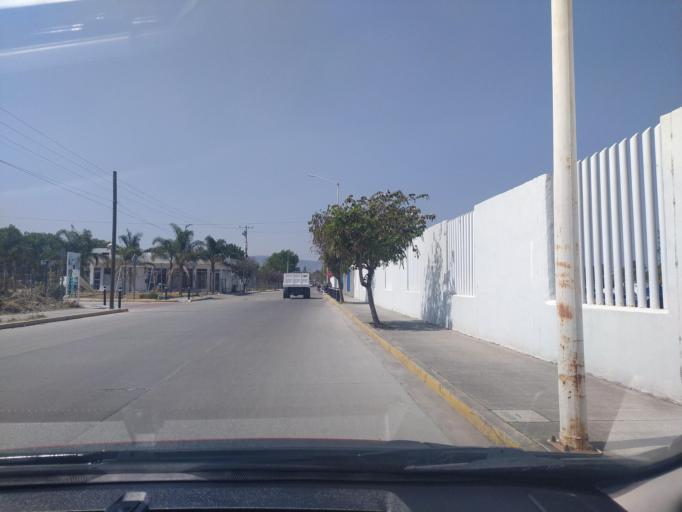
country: MX
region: Guanajuato
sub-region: San Francisco del Rincon
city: Estacion de San Francisco
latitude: 21.0232
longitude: -101.8271
